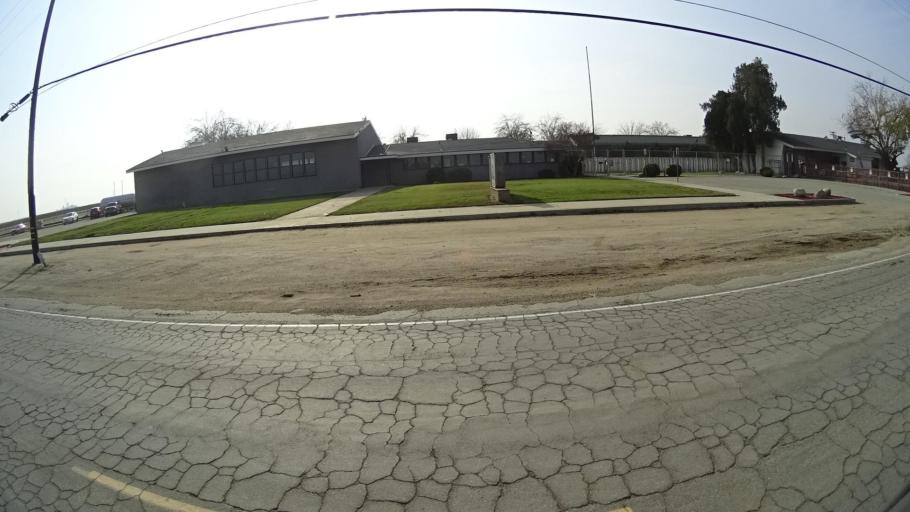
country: US
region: California
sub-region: Kern County
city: Weedpatch
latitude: 35.0930
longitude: -118.9162
